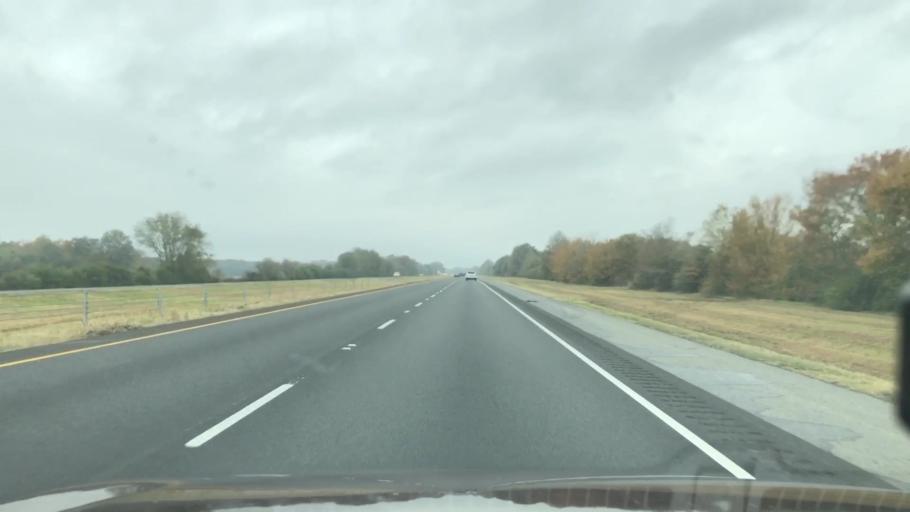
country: US
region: Louisiana
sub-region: Richland Parish
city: Rayville
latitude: 32.4612
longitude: -91.7817
